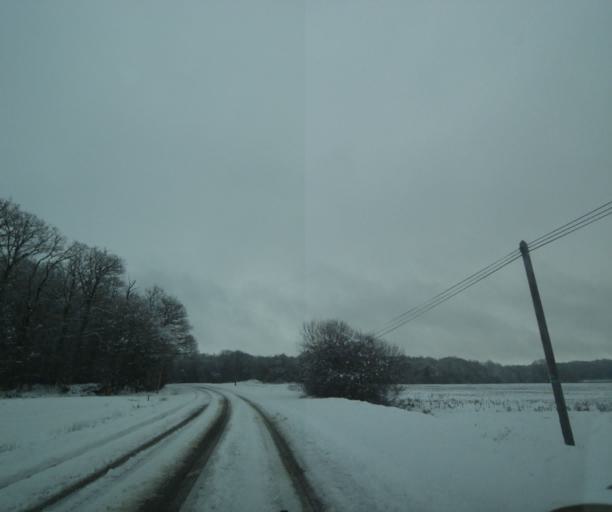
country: FR
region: Champagne-Ardenne
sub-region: Departement de la Haute-Marne
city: Montier-en-Der
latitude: 48.5454
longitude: 4.7998
